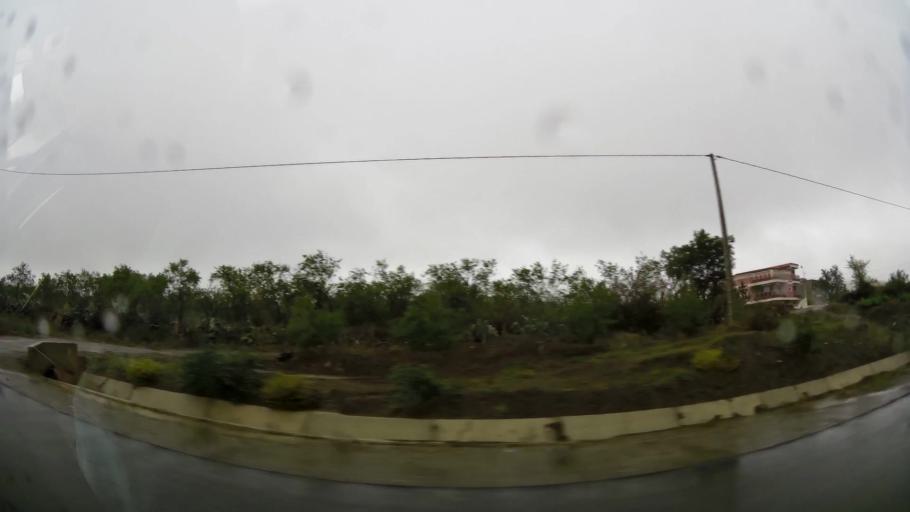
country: MA
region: Oriental
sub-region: Nador
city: Midar
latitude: 34.8478
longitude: -3.7216
